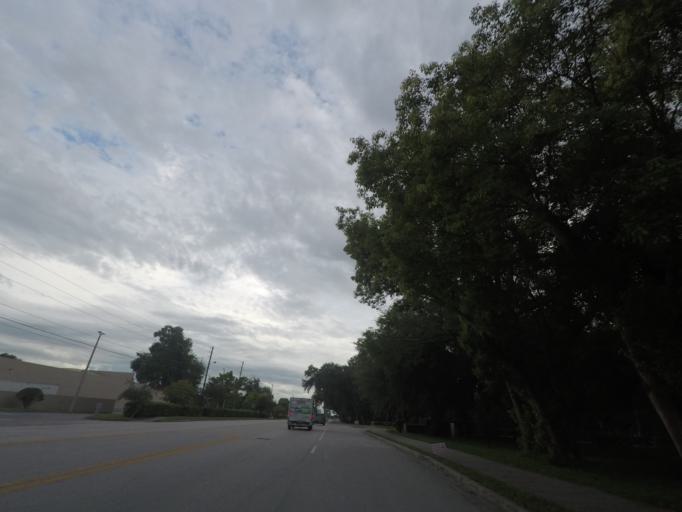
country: US
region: Florida
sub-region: Osceola County
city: Kissimmee
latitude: 28.3078
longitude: -81.4450
